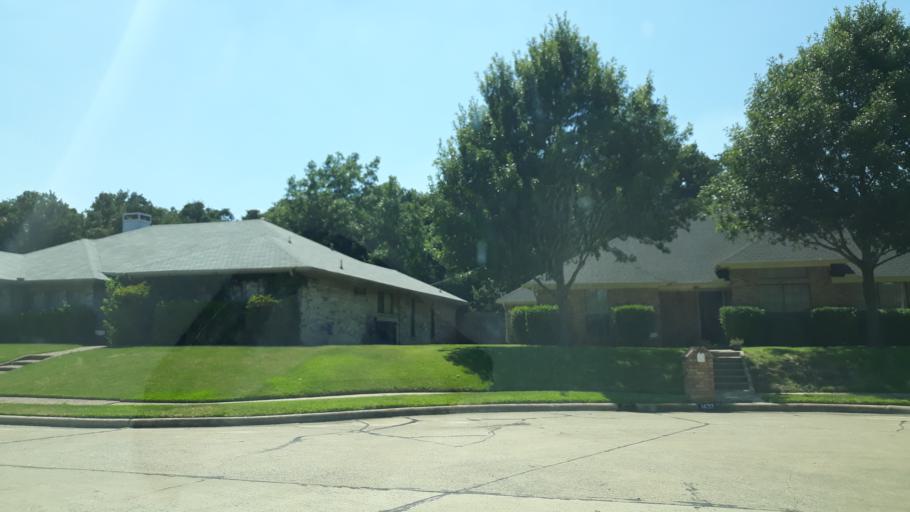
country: US
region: Texas
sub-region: Dallas County
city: Irving
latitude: 32.8294
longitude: -97.0057
